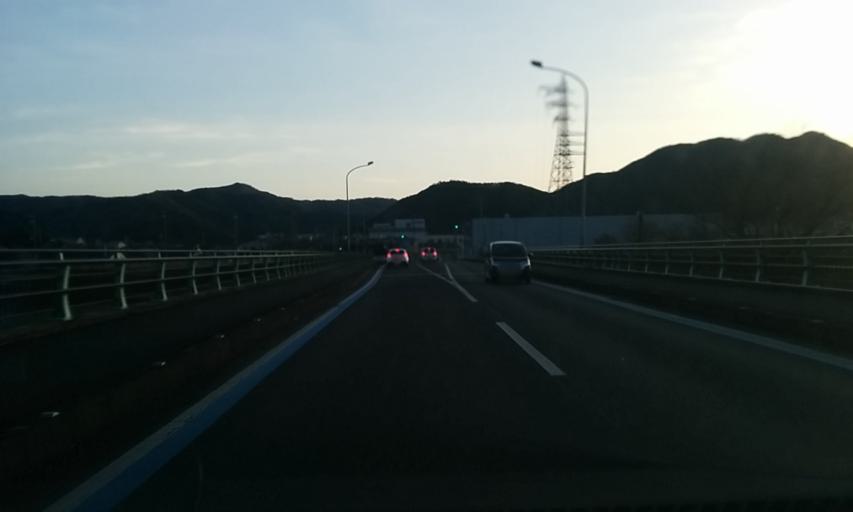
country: JP
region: Kyoto
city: Ayabe
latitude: 35.3093
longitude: 135.2588
